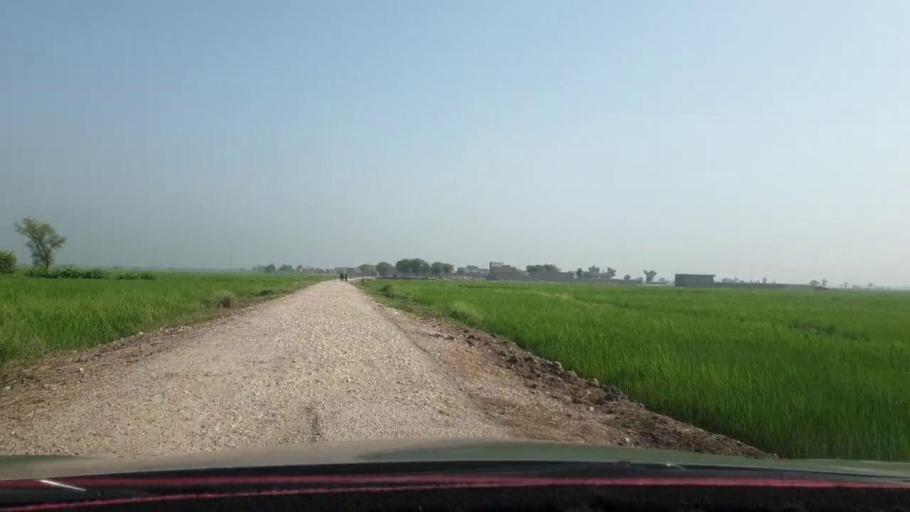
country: PK
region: Sindh
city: Nasirabad
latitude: 27.4717
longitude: 67.9232
